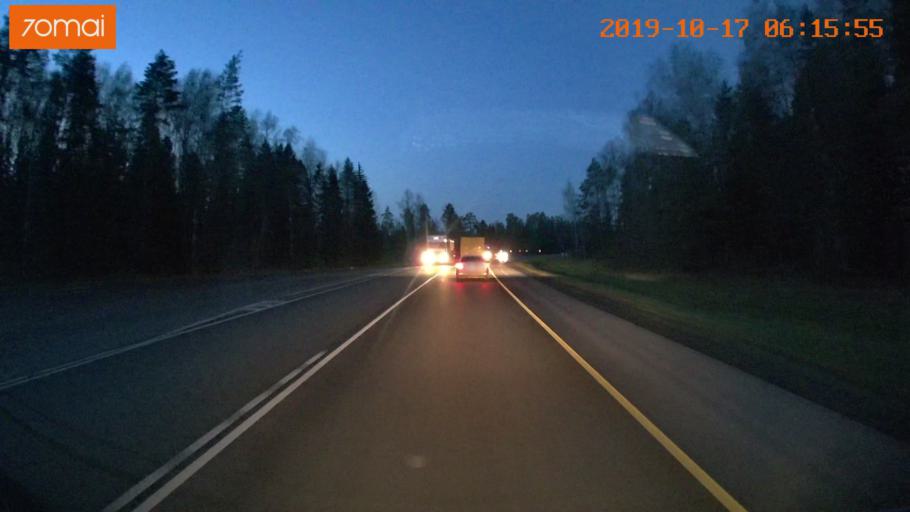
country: RU
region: Ivanovo
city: Lezhnevo
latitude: 56.8668
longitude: 40.9375
